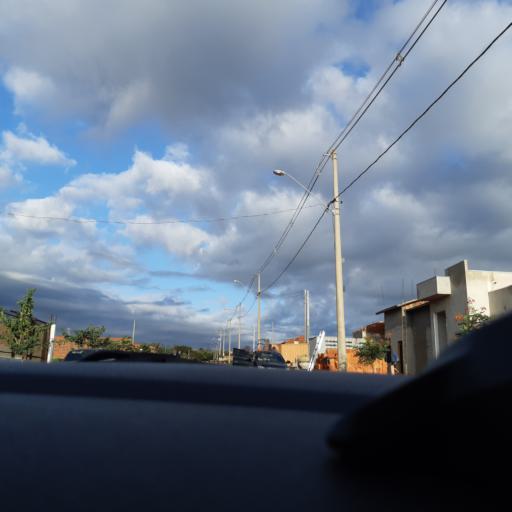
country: BR
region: Sao Paulo
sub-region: Ourinhos
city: Ourinhos
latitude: -23.0036
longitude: -49.8420
